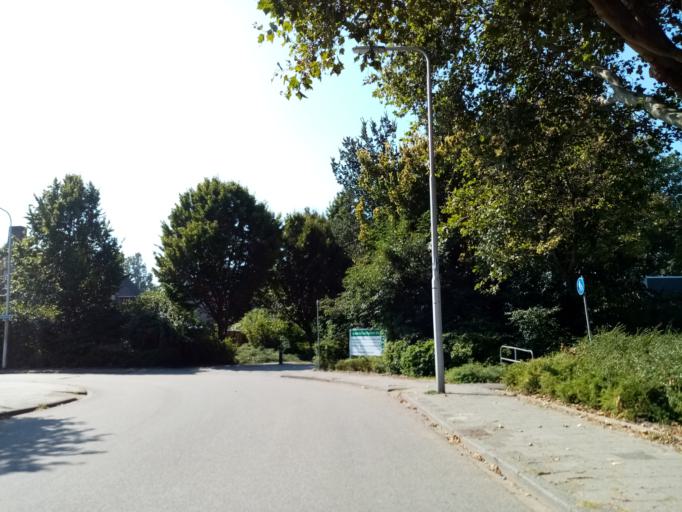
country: NL
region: South Holland
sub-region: Gemeente Lisse
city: Lisse
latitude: 52.2485
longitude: 4.5603
